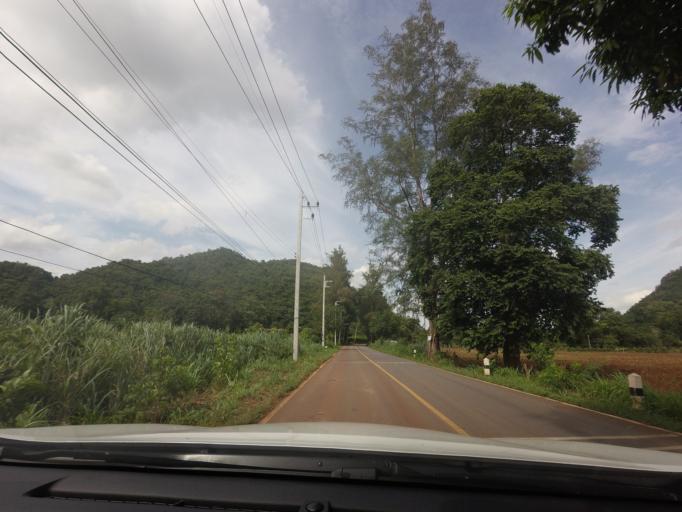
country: TH
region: Nakhon Ratchasima
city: Pak Chong
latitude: 14.5456
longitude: 101.4140
